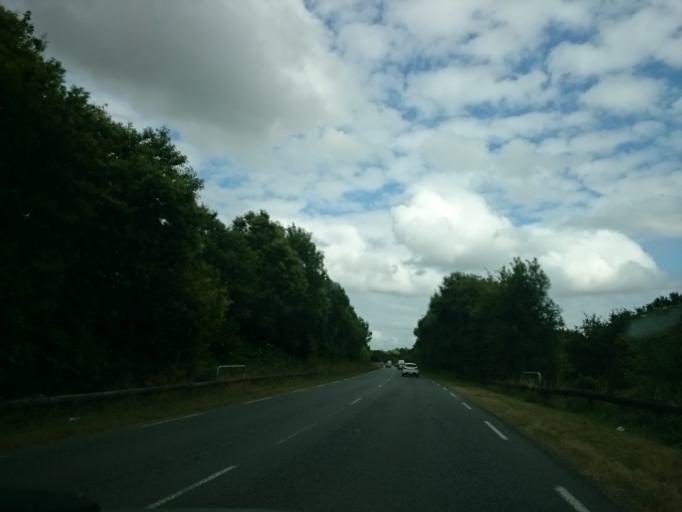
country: FR
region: Brittany
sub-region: Departement du Finistere
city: Gouesnou
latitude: 48.4387
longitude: -4.4549
